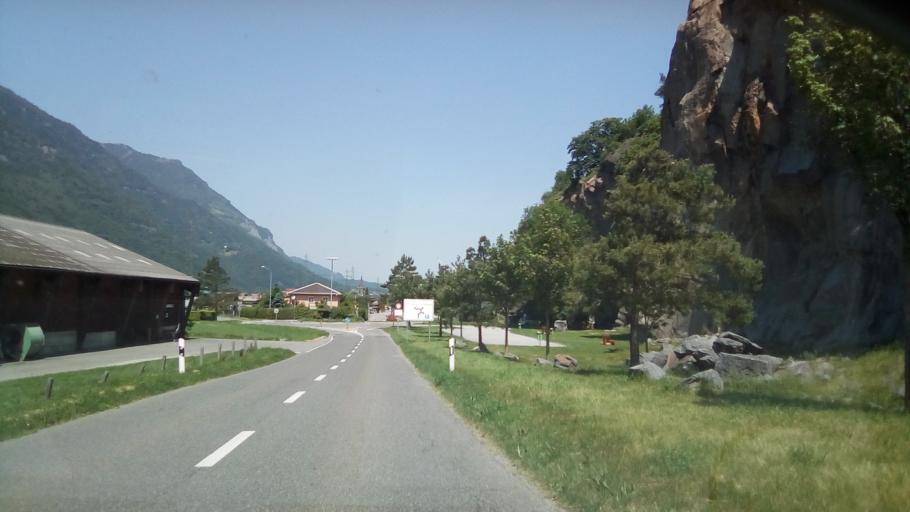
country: CH
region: Valais
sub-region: Saint-Maurice District
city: Vernayaz
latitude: 46.1436
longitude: 7.0457
